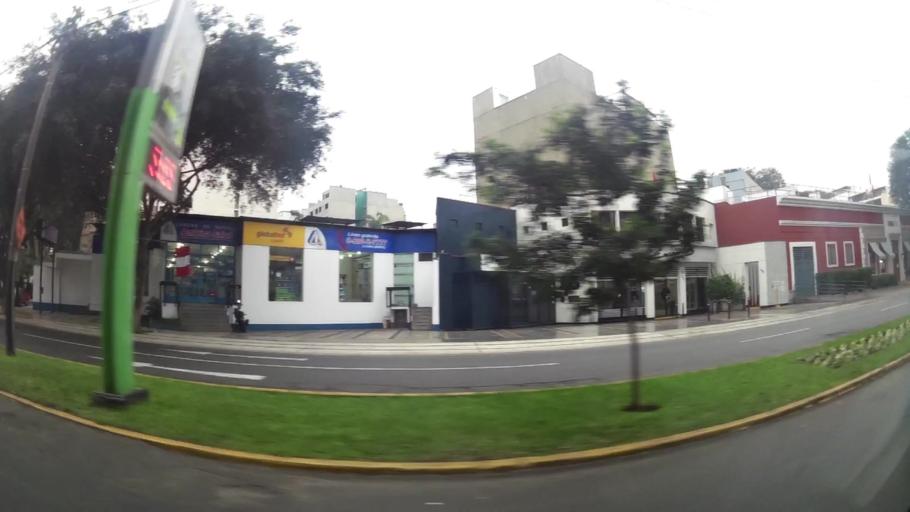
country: PE
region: Lima
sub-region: Lima
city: Surco
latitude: -12.1329
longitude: -77.0283
